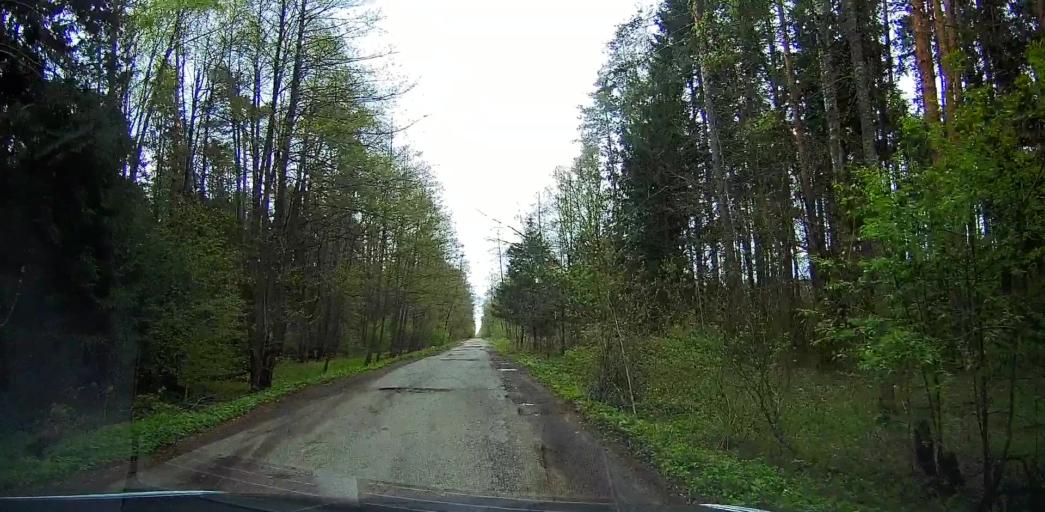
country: RU
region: Moskovskaya
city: Malyshevo
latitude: 55.5530
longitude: 38.3440
